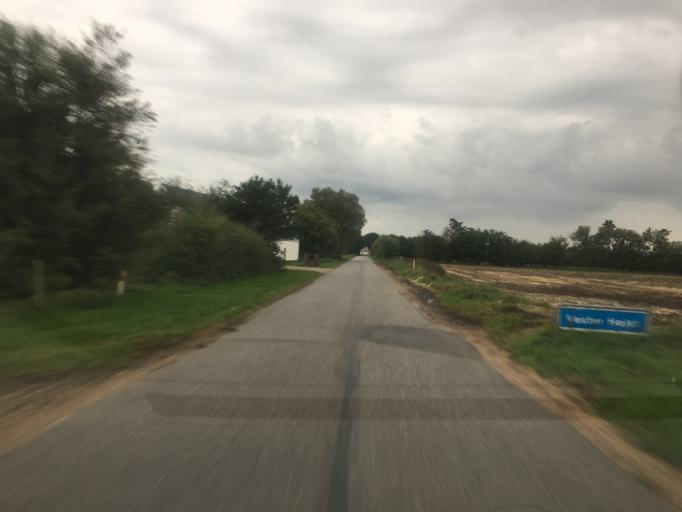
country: DK
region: South Denmark
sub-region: Tonder Kommune
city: Logumkloster
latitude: 55.0114
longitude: 9.0346
